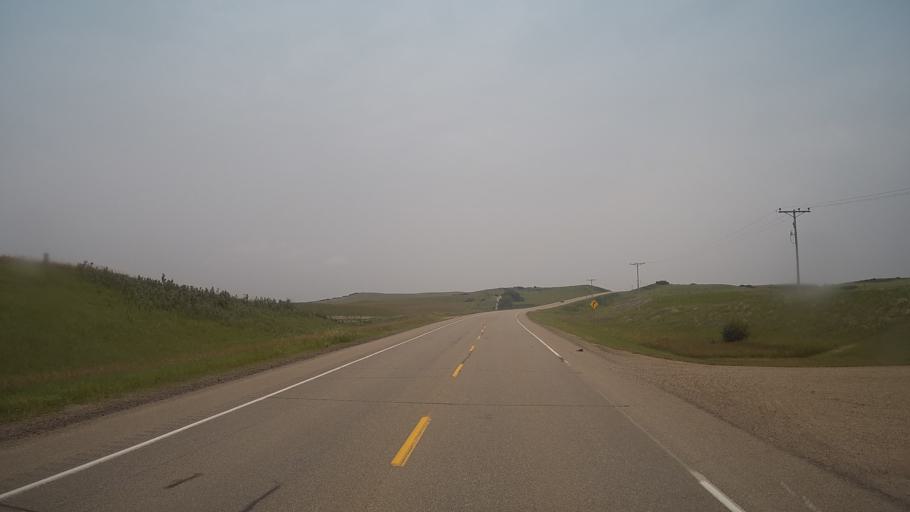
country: CA
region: Saskatchewan
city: Biggar
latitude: 52.0565
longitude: -107.8683
